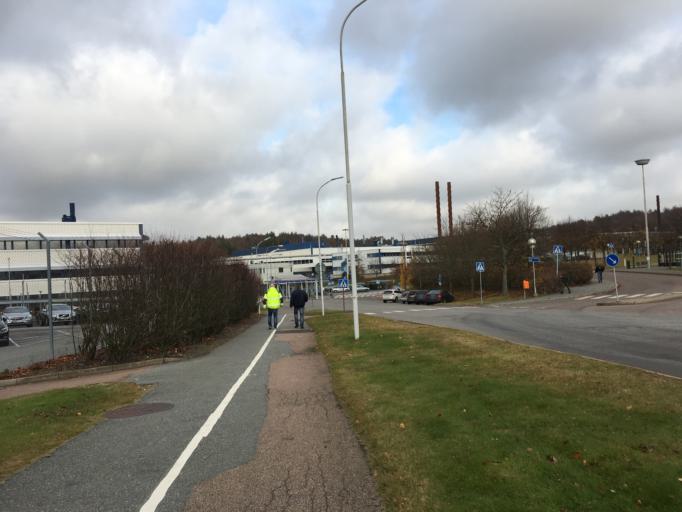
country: SE
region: Vaestra Goetaland
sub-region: Goteborg
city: Majorna
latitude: 57.7278
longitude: 11.8593
